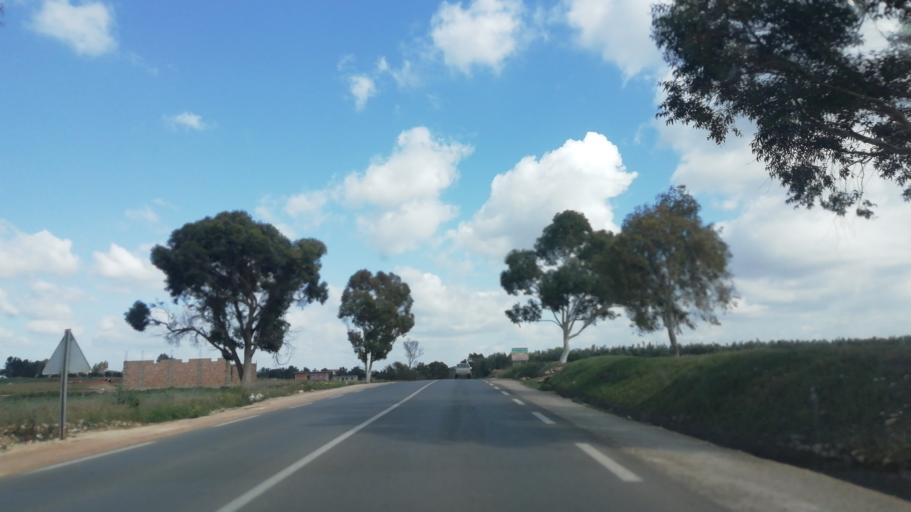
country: DZ
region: Relizane
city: Relizane
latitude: 35.7160
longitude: 0.3020
